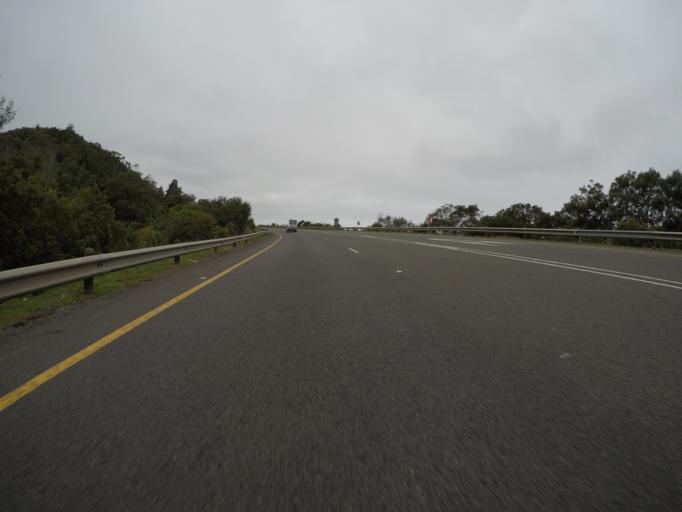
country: ZA
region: Western Cape
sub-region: Eden District Municipality
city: Plettenberg Bay
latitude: -34.0074
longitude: 23.4131
